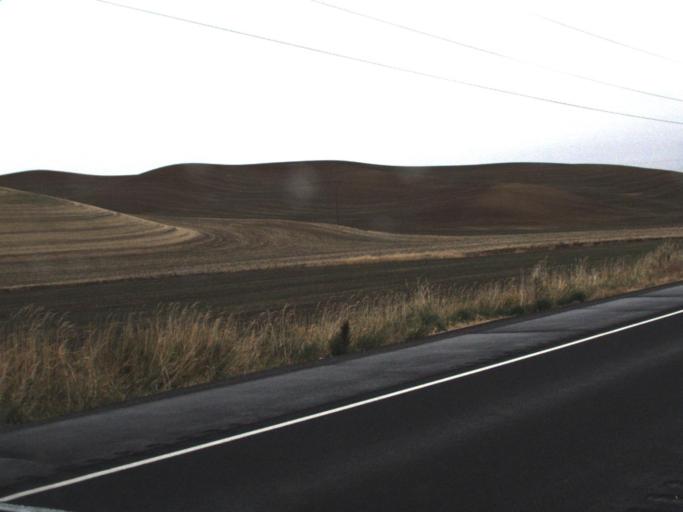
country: US
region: Washington
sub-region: Whitman County
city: Colfax
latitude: 46.8184
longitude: -117.3229
